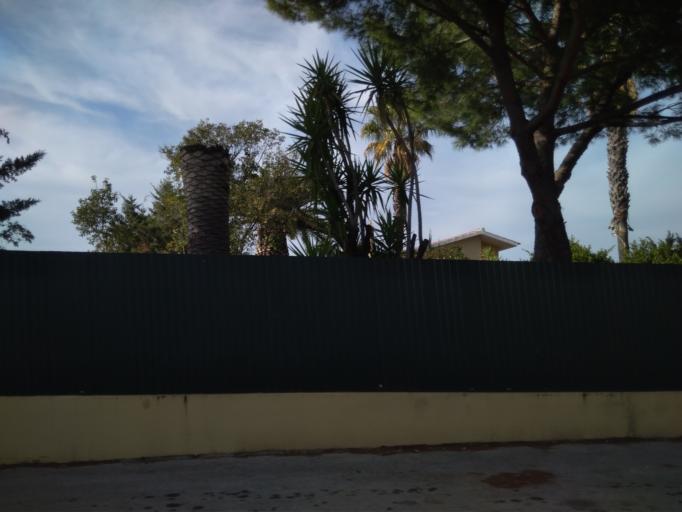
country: PT
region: Faro
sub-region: Faro
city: Santa Barbara de Nexe
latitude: 37.0895
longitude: -7.9115
